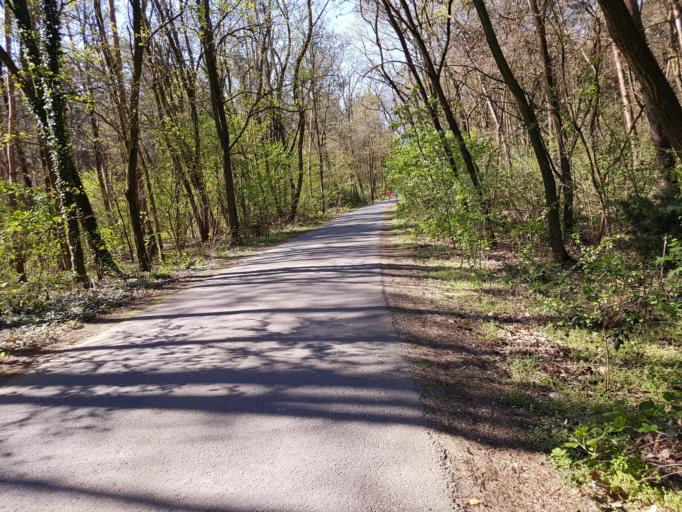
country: DE
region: Brandenburg
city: Groden
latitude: 51.3987
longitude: 13.5640
